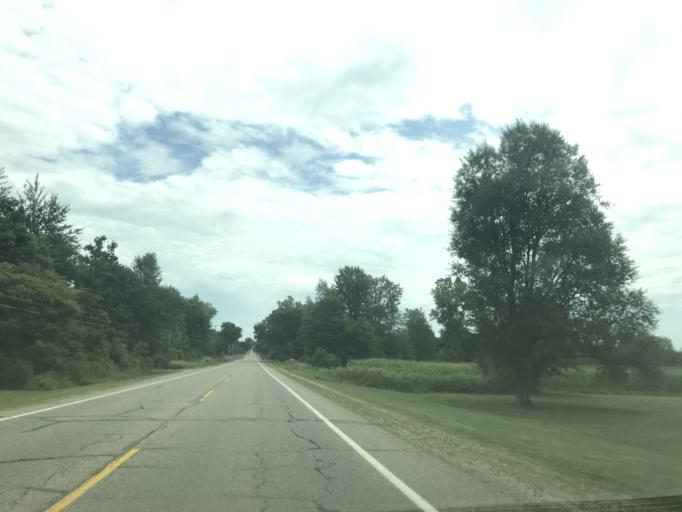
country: US
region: Michigan
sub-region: Clinton County
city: Wacousta
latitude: 42.7935
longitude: -84.7164
